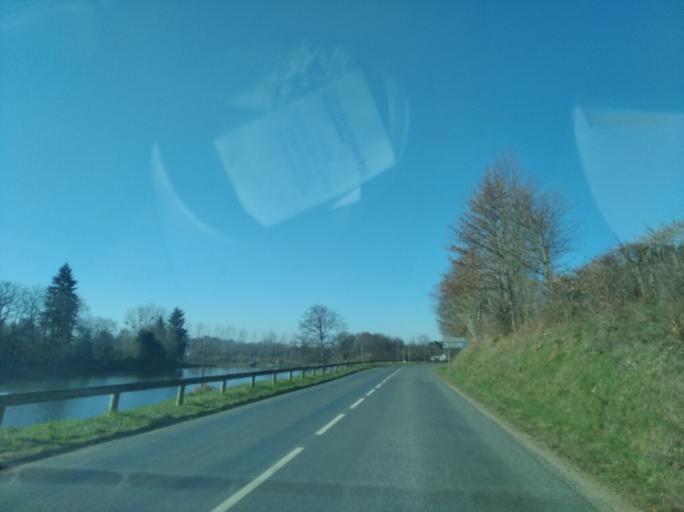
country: FR
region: Auvergne
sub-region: Departement de l'Allier
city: Le Mayet-de-Montagne
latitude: 46.0617
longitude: 3.6715
